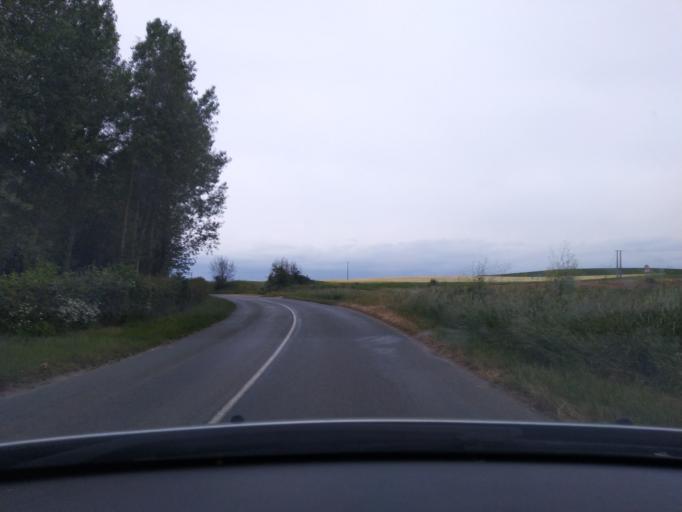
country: FR
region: Nord-Pas-de-Calais
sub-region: Departement du Pas-de-Calais
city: Marquise
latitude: 50.8416
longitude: 1.6842
